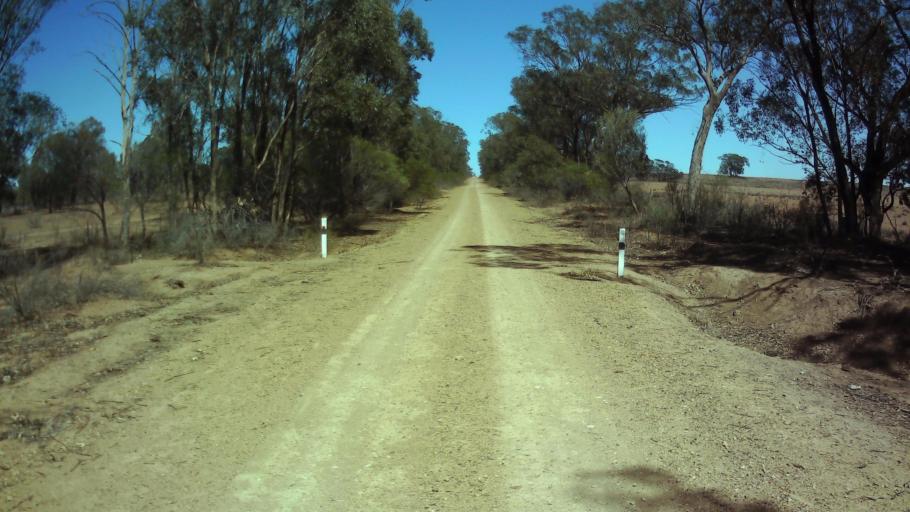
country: AU
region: New South Wales
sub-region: Forbes
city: Forbes
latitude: -33.6961
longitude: 147.8430
